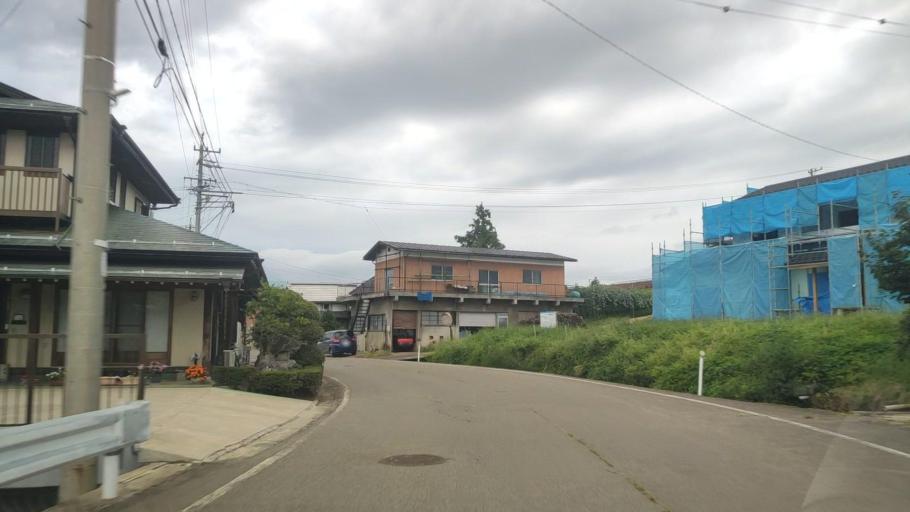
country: JP
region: Nagano
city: Nakano
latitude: 36.7805
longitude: 138.3734
